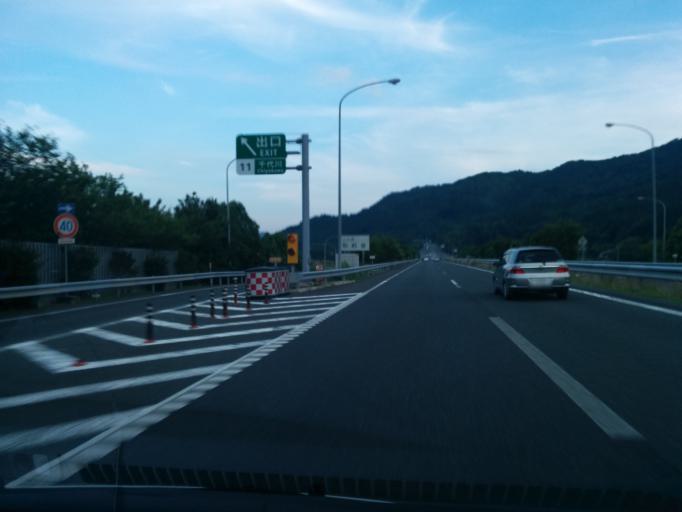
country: JP
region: Kyoto
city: Kameoka
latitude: 35.0532
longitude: 135.5346
